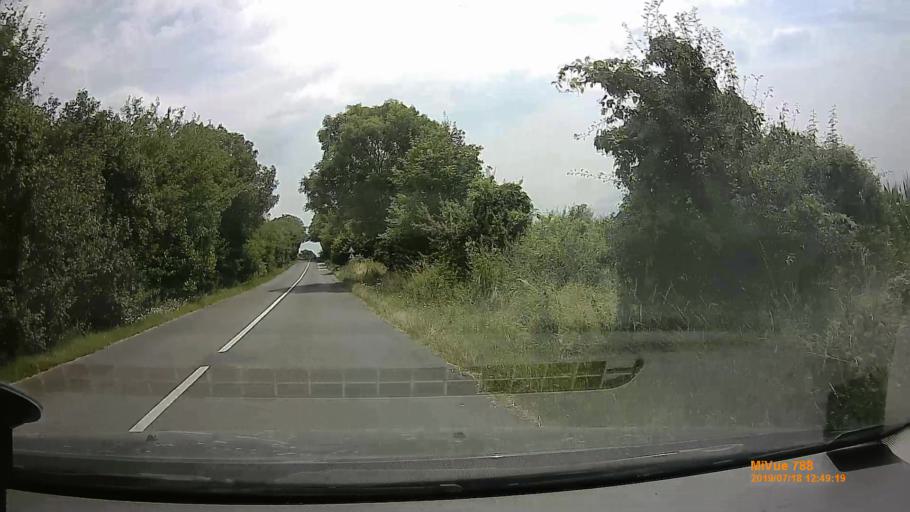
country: HU
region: Pest
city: Perbal
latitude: 47.5766
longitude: 18.7778
